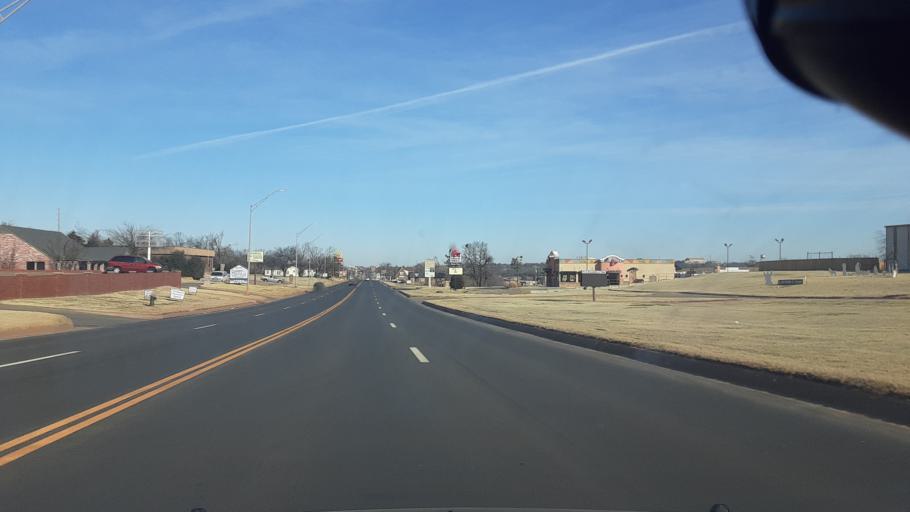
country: US
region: Oklahoma
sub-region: Logan County
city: Guthrie
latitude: 35.8573
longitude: -97.4254
